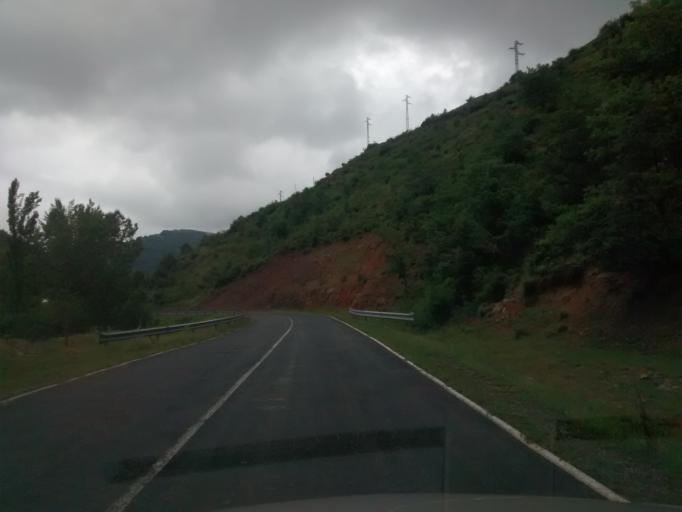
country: ES
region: La Rioja
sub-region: Provincia de La Rioja
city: Ajamil
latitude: 42.1724
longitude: -2.4853
